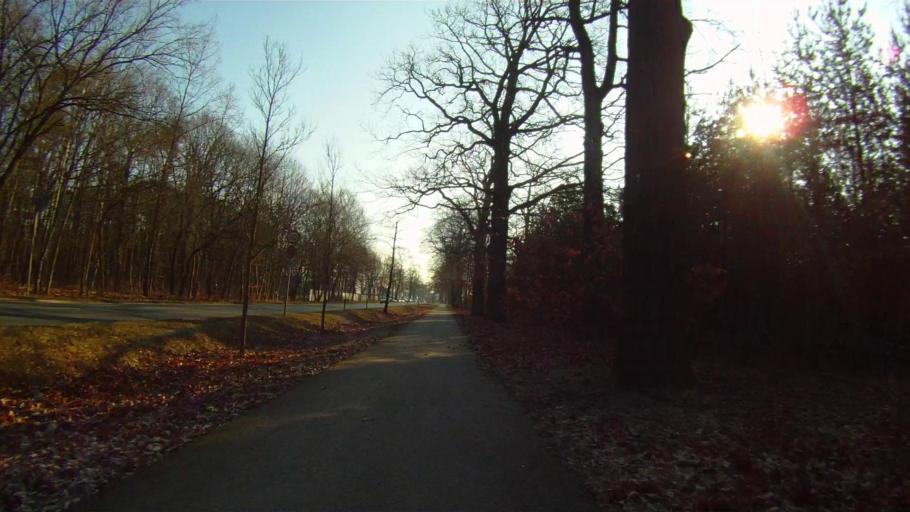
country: DE
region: Brandenburg
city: Erkner
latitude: 52.4295
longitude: 13.7361
